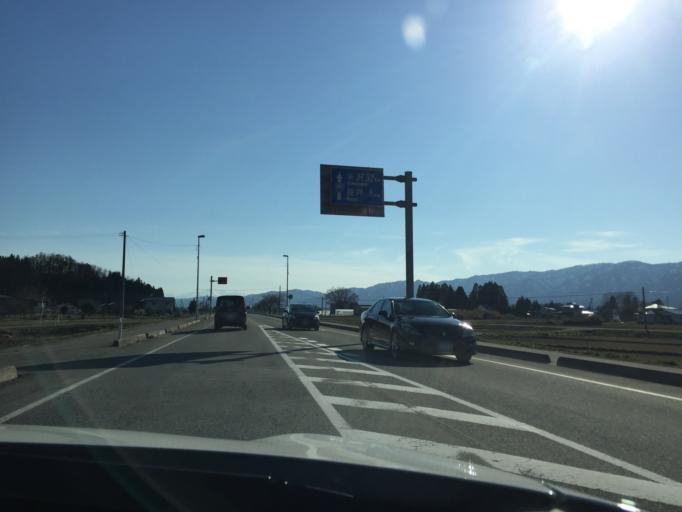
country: JP
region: Yamagata
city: Nagai
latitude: 38.1568
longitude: 140.0709
